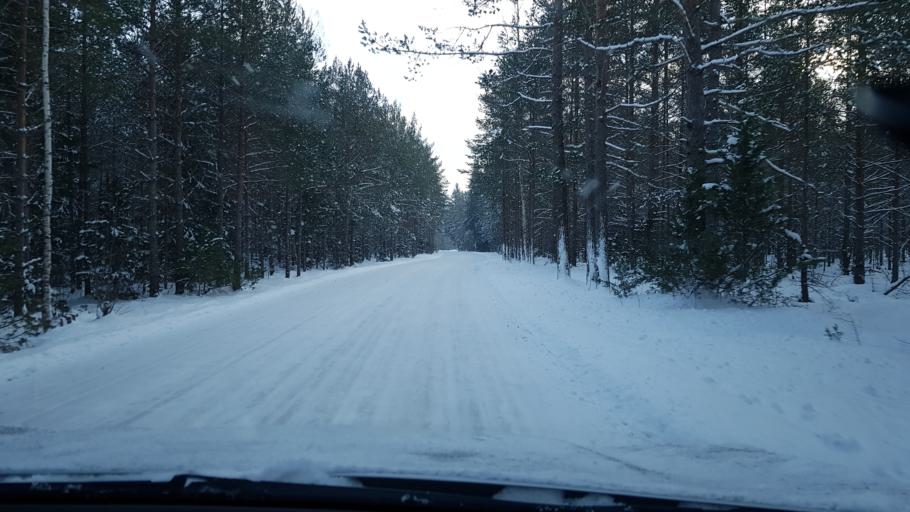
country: EE
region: Harju
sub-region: Nissi vald
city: Turba
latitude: 59.1758
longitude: 24.1325
